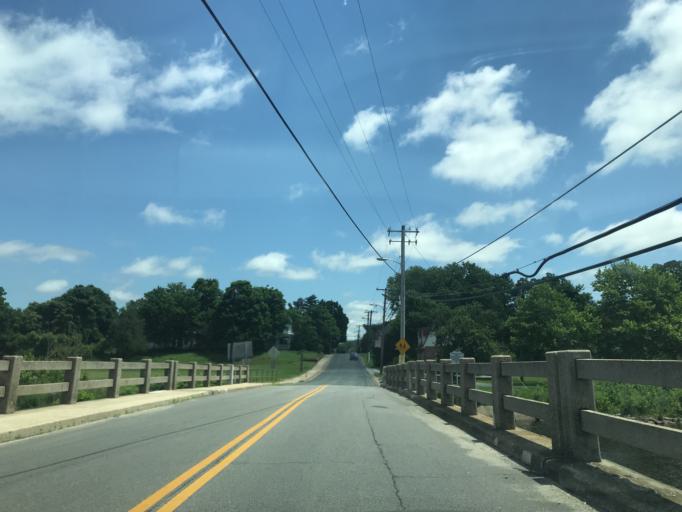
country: US
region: Maryland
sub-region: Caroline County
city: Federalsburg
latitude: 38.6945
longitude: -75.7725
